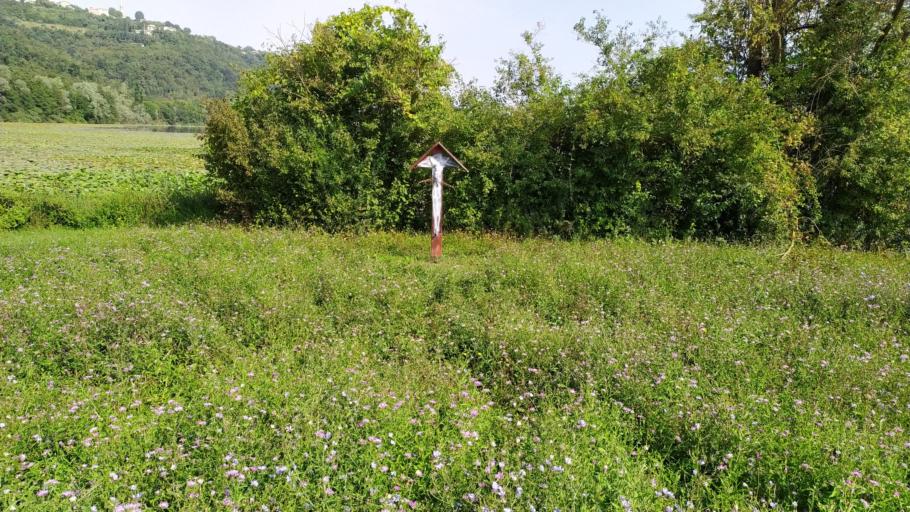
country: IT
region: Veneto
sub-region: Provincia di Vicenza
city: Arcugnano-Torri
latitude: 45.4633
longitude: 11.5425
